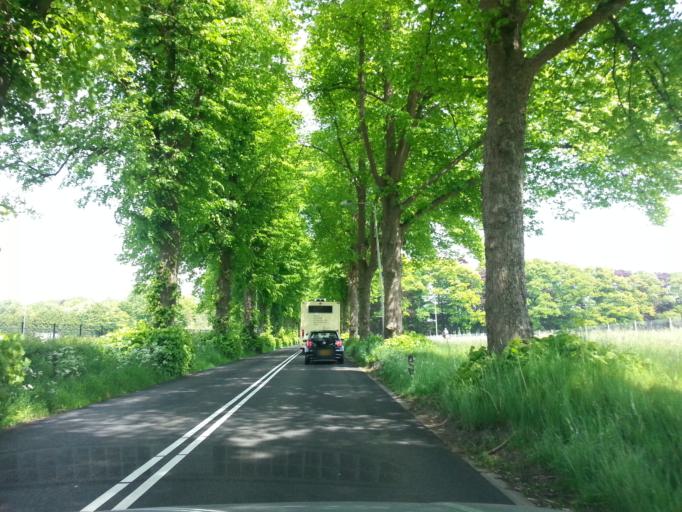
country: NL
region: Gelderland
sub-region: Gemeente Arnhem
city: Hoogkamp
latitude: 52.0013
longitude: 5.8831
